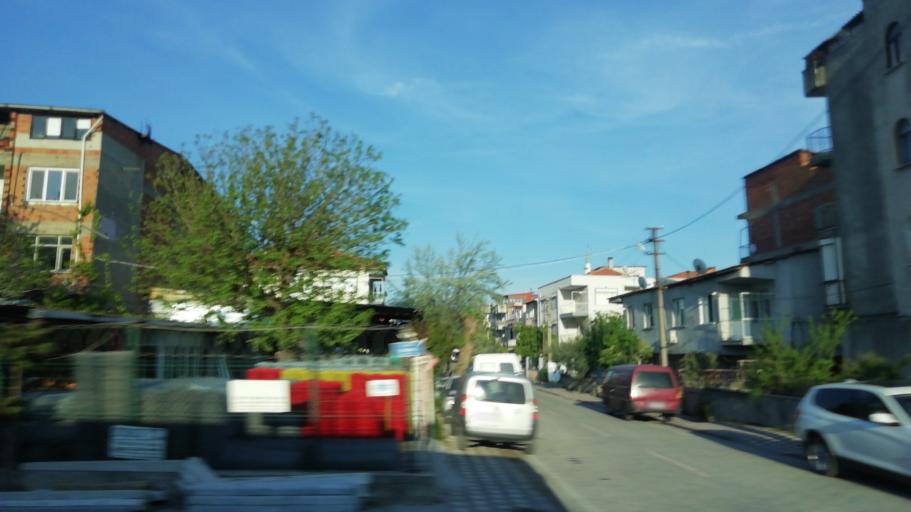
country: TR
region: Manisa
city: Akhisar
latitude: 38.9302
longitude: 27.8346
